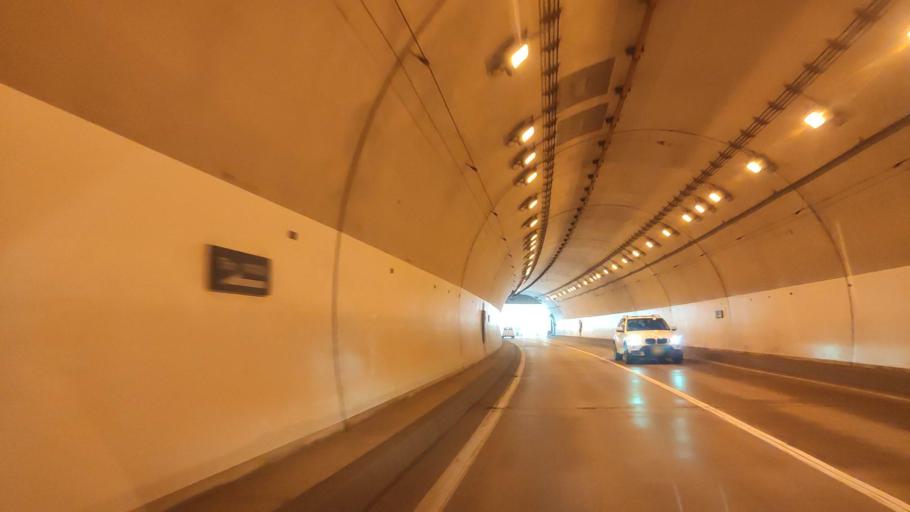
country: JP
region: Hokkaido
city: Rumoi
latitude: 43.6741
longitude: 141.3468
